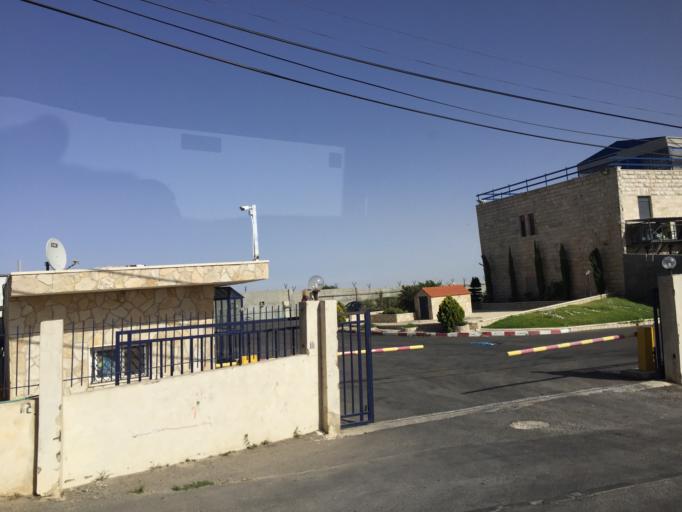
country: PS
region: West Bank
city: Bayt Jala
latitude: 31.7143
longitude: 35.1758
